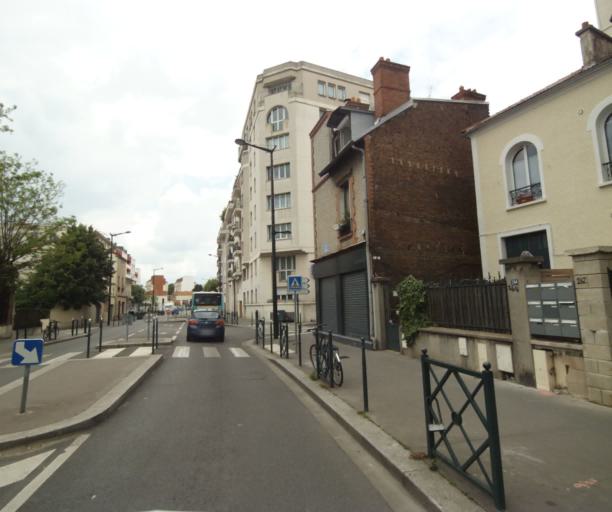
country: FR
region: Ile-de-France
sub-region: Departement des Hauts-de-Seine
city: Bois-Colombes
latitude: 48.9220
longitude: 2.2775
